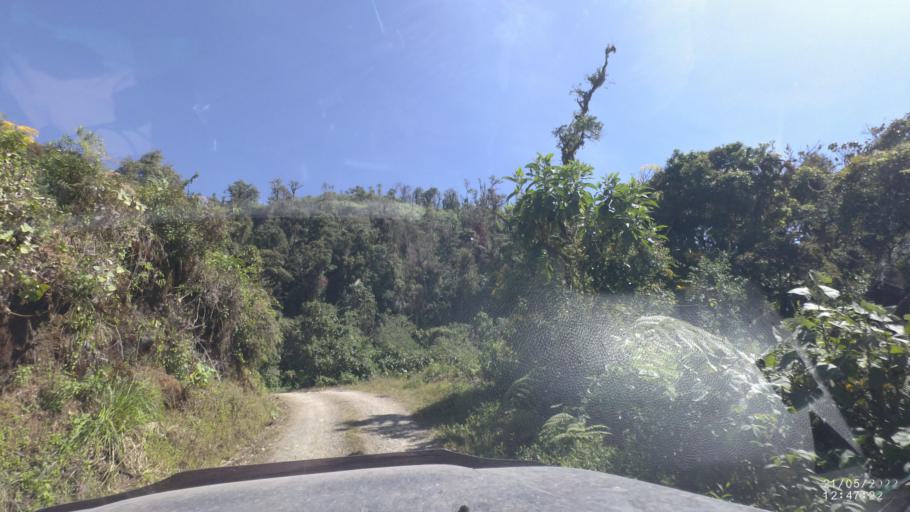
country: BO
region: Cochabamba
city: Colomi
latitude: -17.1828
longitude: -65.9415
